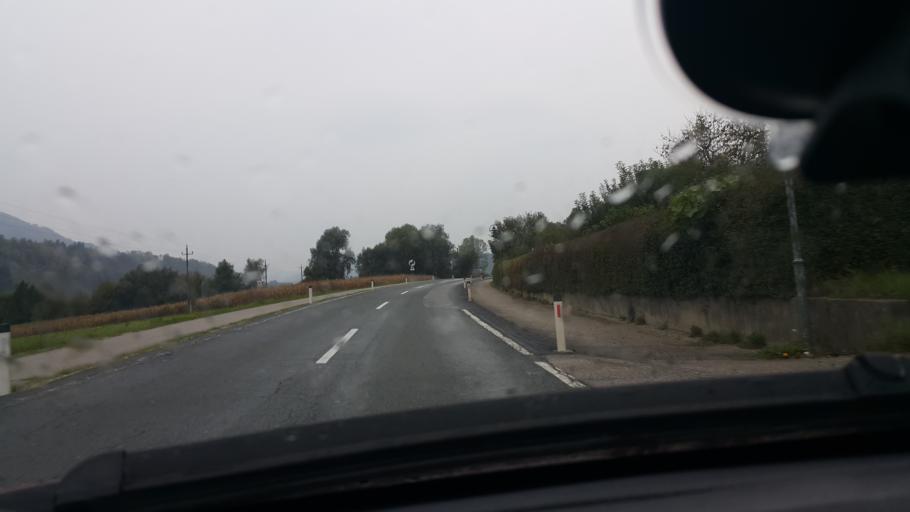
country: AT
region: Carinthia
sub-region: Politischer Bezirk Wolfsberg
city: Lavamund
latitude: 46.6329
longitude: 14.9608
